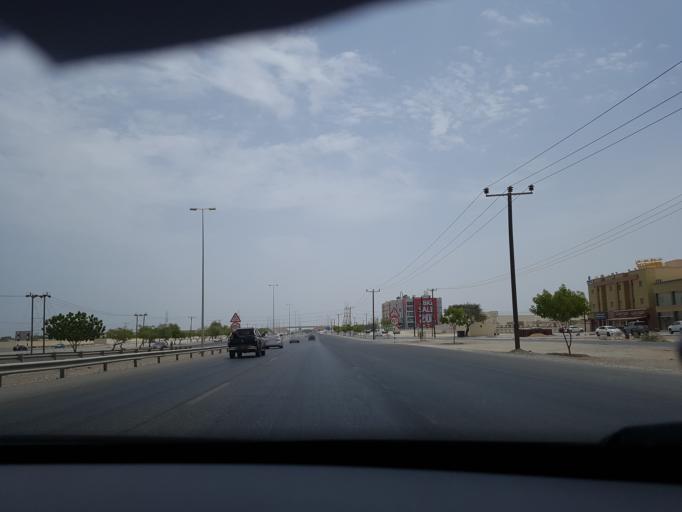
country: OM
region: Al Batinah
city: Barka'
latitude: 23.6759
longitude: 57.9953
